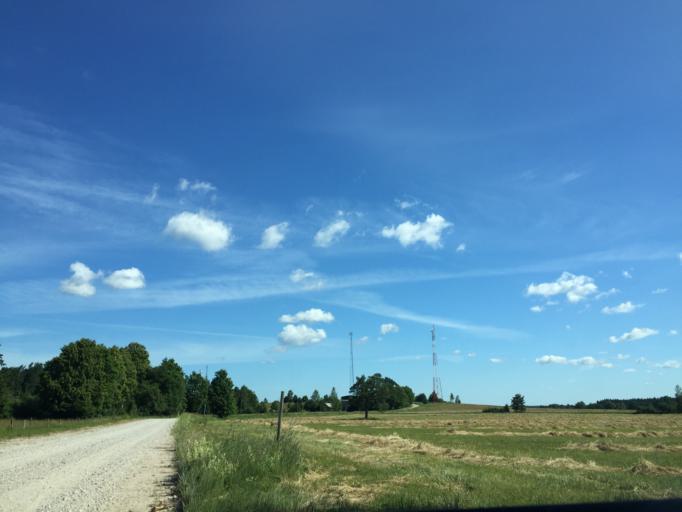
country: LV
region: Dundaga
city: Dundaga
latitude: 57.3525
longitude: 22.0274
